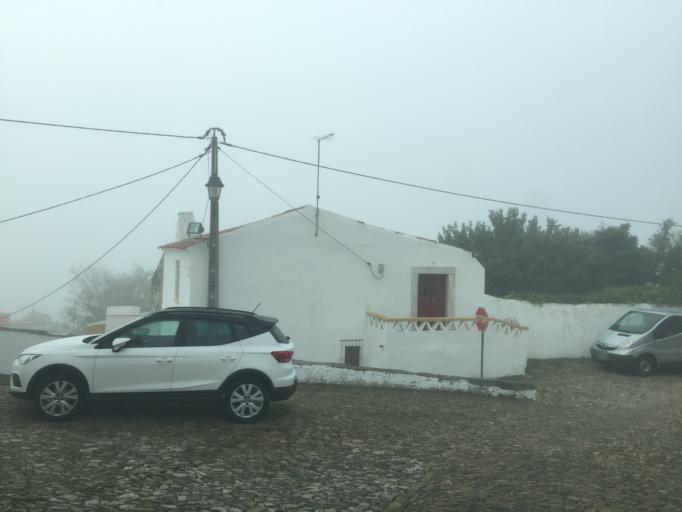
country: PT
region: Portalegre
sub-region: Alter do Chao
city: Alter do Chao
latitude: 39.1341
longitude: -7.5864
